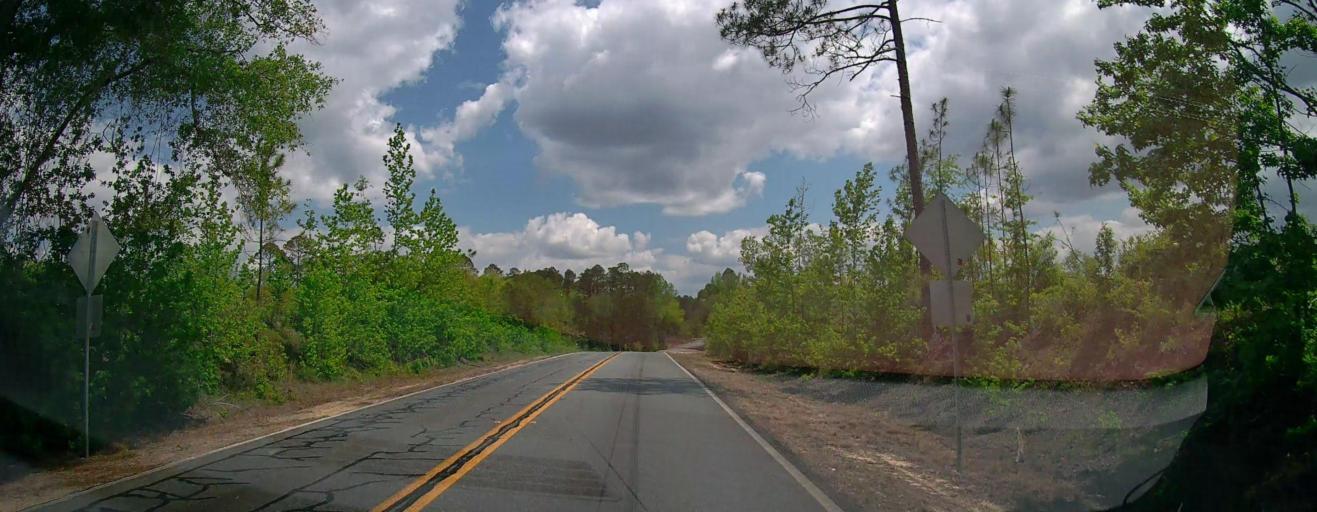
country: US
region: Georgia
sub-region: Treutlen County
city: Soperton
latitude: 32.5009
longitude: -82.6154
